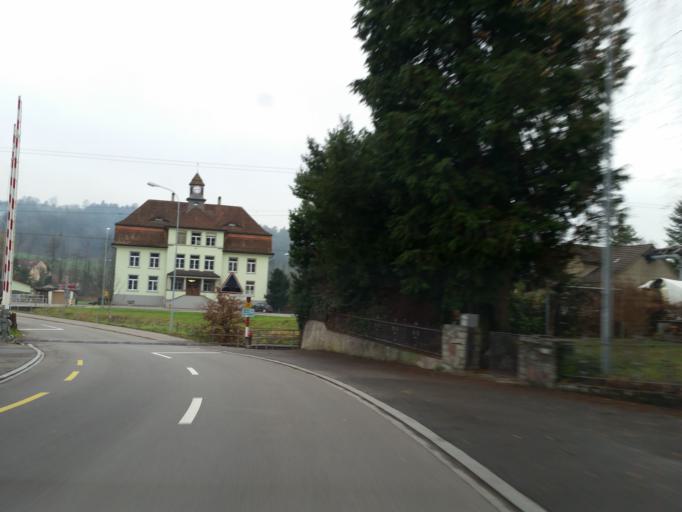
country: CH
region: Thurgau
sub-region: Weinfelden District
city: Sulgen
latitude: 47.5267
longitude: 9.1998
